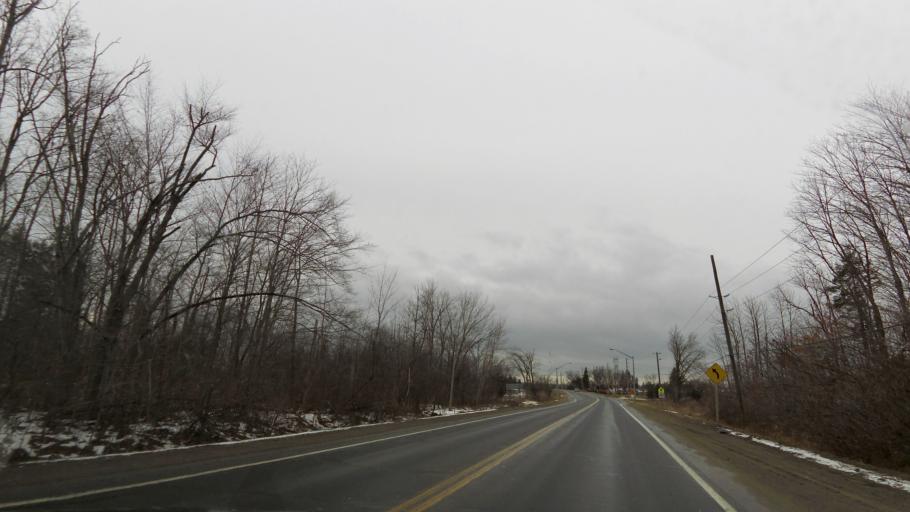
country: CA
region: Ontario
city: Vaughan
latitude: 43.8406
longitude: -79.6672
